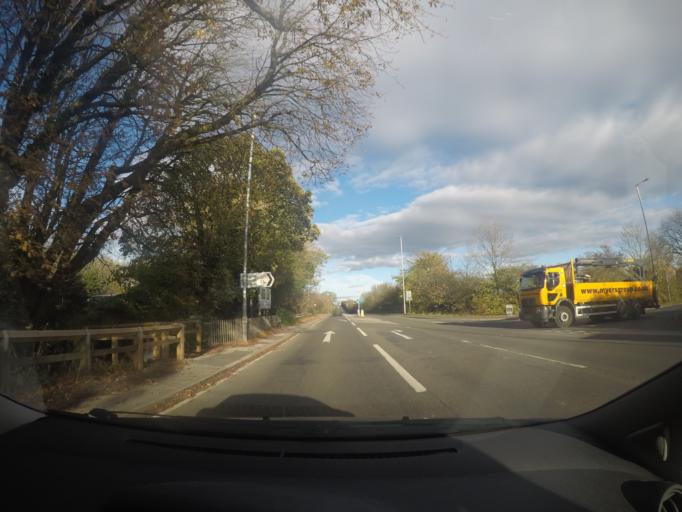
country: GB
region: England
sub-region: City and Borough of Leeds
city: Scholes
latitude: 53.8350
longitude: -1.4351
